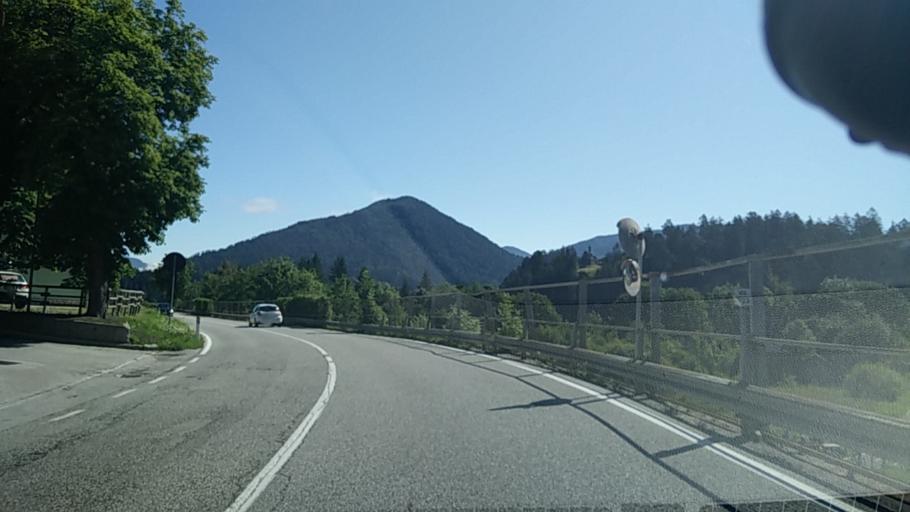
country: IT
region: Friuli Venezia Giulia
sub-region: Provincia di Udine
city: Tarvisio
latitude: 46.5079
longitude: 13.5991
